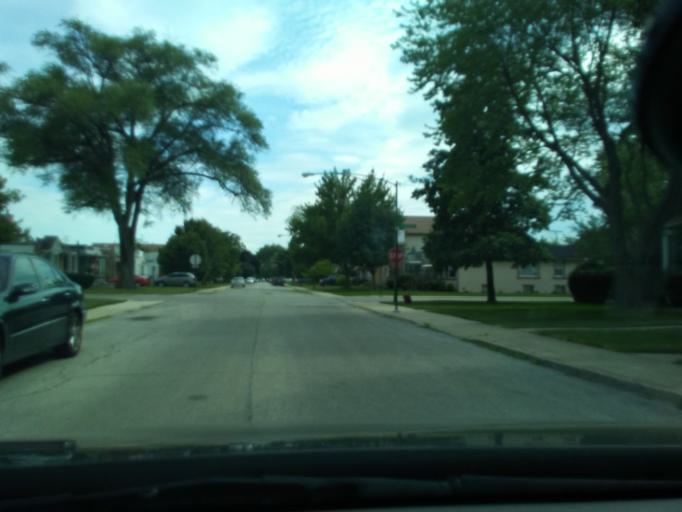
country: US
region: Illinois
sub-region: Cook County
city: Harwood Heights
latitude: 41.9742
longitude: -87.7855
